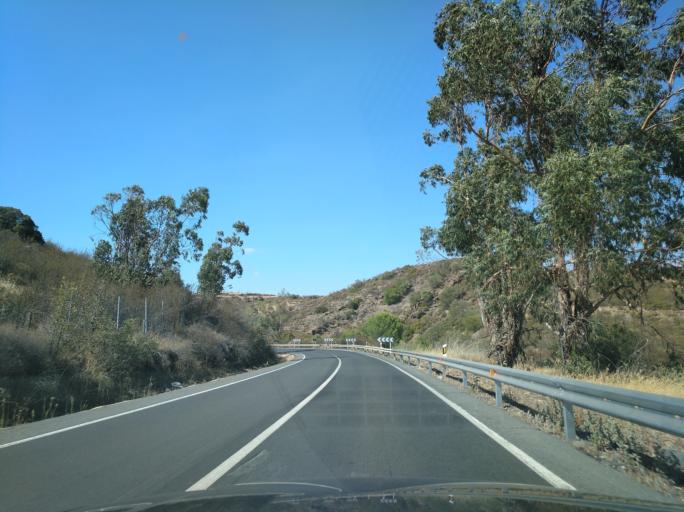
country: ES
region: Andalusia
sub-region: Provincia de Huelva
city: San Bartolome de la Torre
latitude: 37.4759
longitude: -7.1258
